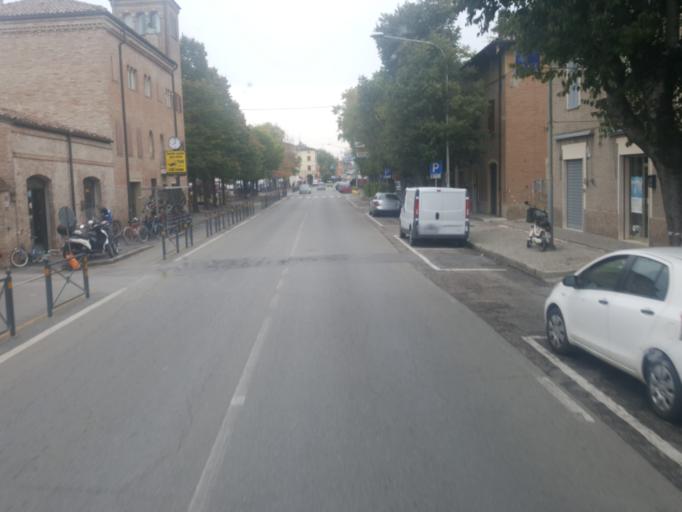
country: IT
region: Emilia-Romagna
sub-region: Provincia di Modena
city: Nonantola
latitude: 44.6784
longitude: 11.0448
